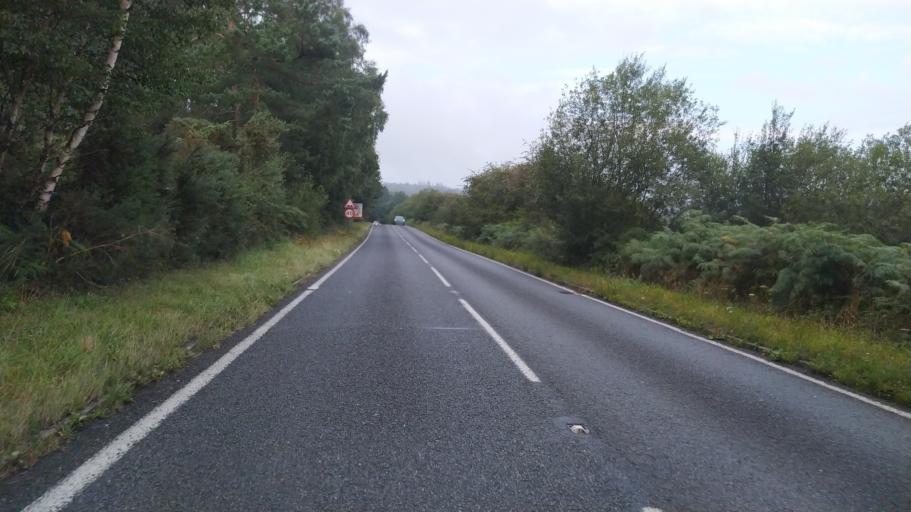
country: GB
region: England
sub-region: Hampshire
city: New Milton
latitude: 50.8077
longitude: -1.6685
